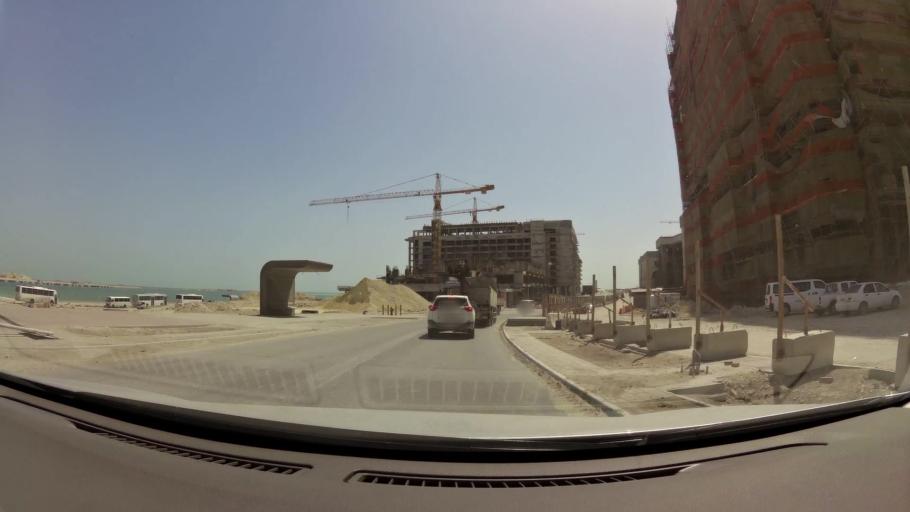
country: QA
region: Baladiyat Umm Salal
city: Umm Salal Muhammad
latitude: 25.4069
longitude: 51.5200
